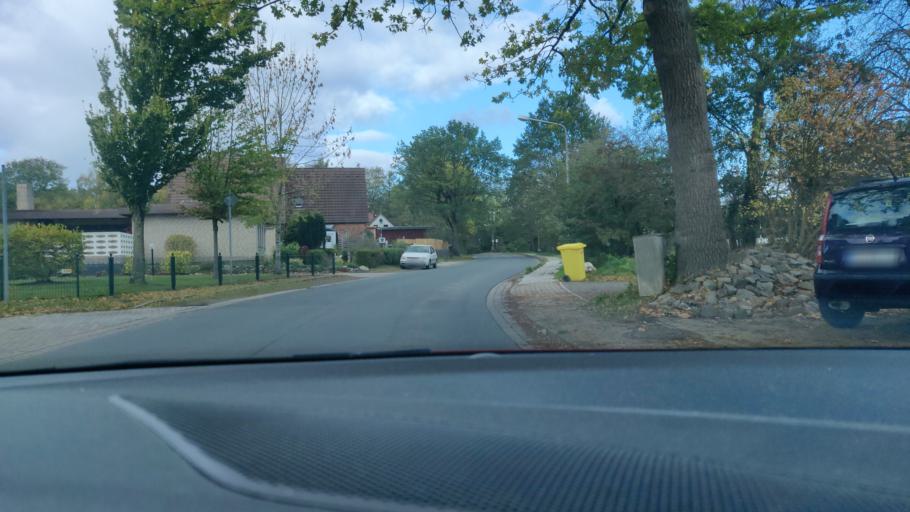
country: DE
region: Lower Saxony
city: Cuxhaven
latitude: 53.8423
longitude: 8.6443
